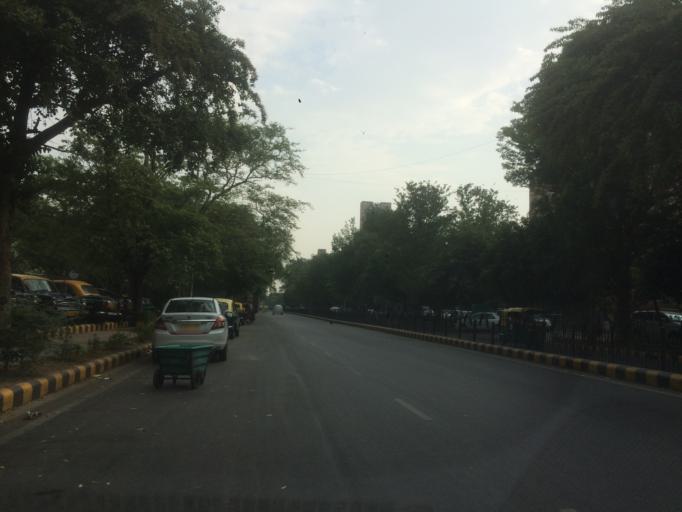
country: IN
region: NCT
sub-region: New Delhi
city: New Delhi
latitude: 28.6209
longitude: 77.2189
